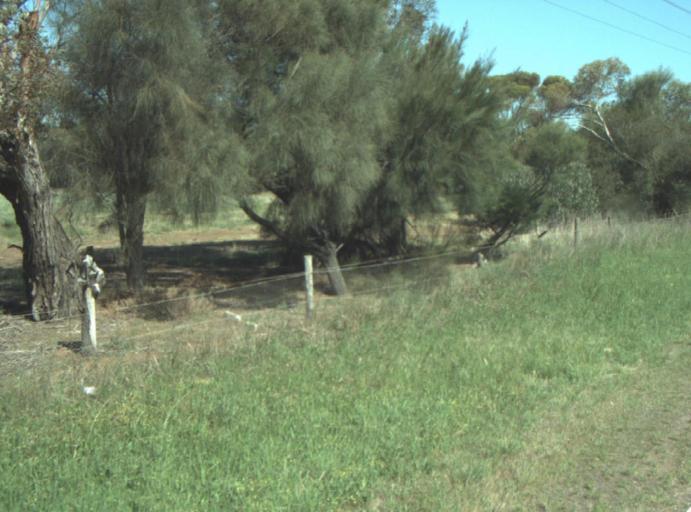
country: AU
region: Victoria
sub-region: Greater Geelong
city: Lara
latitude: -38.0079
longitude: 144.3990
